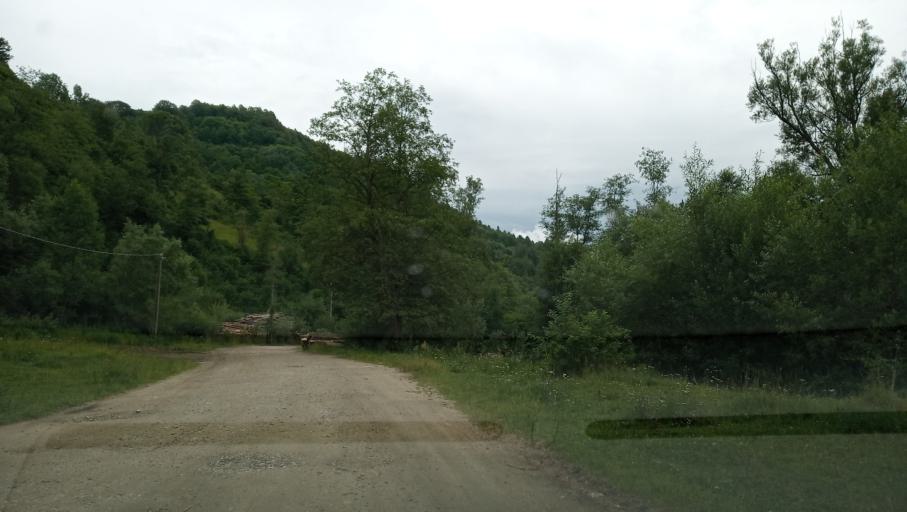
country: RO
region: Hunedoara
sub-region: Oras Petrila
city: Petrila
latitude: 45.4694
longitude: 23.4188
